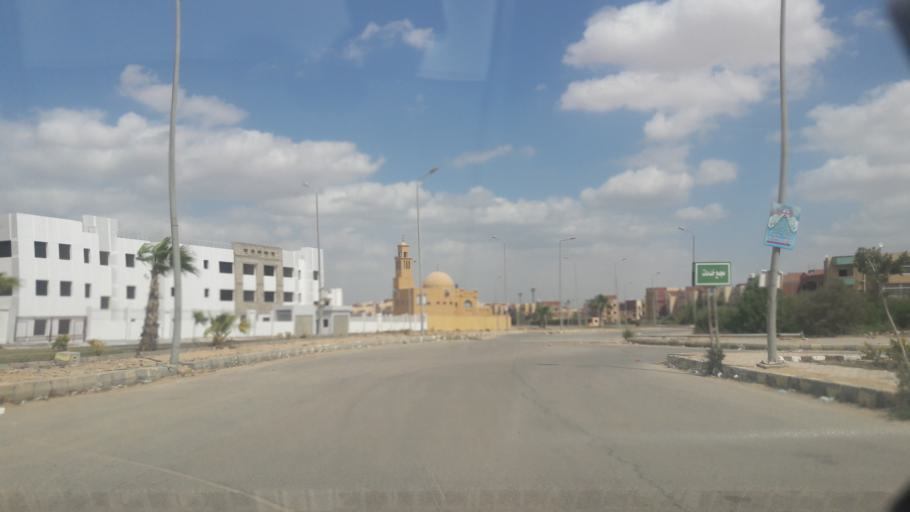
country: EG
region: Al Jizah
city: Madinat Sittah Uktubar
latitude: 29.9339
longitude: 31.0576
